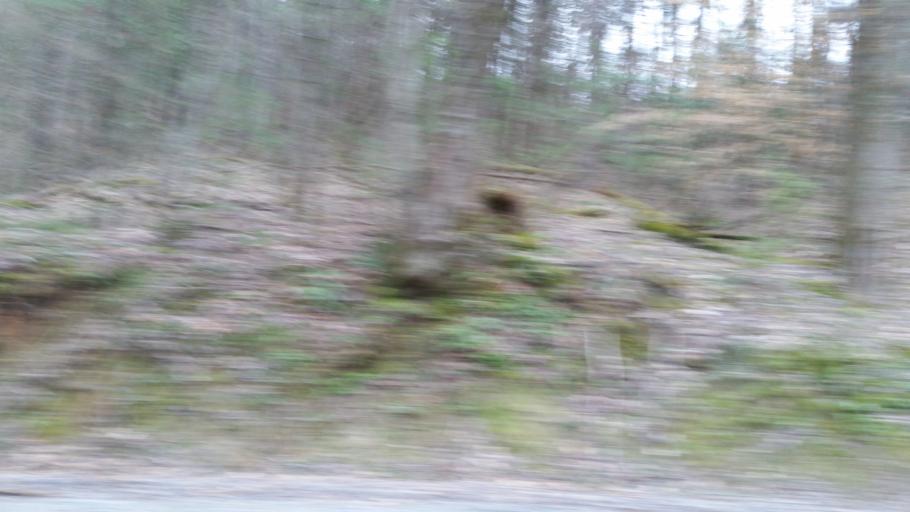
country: US
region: Georgia
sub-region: Fannin County
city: Blue Ridge
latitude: 34.7554
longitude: -84.2589
